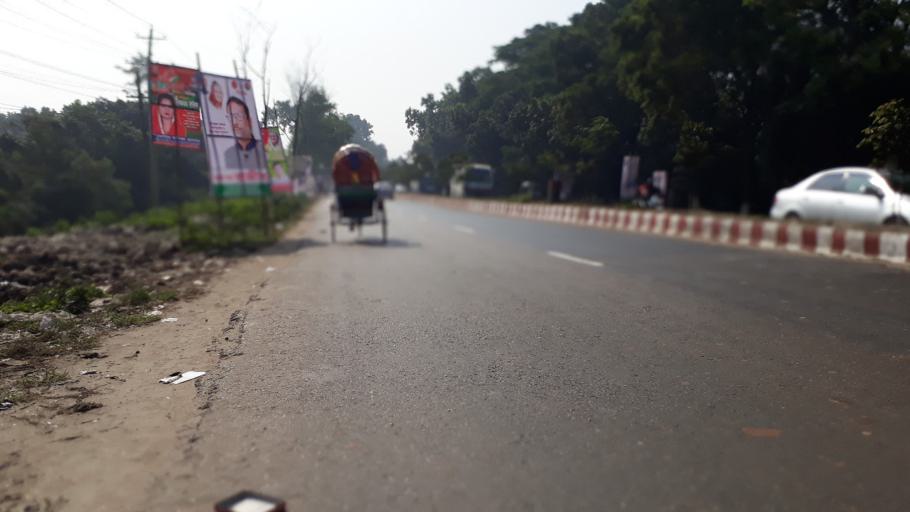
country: BD
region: Dhaka
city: Tungi
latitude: 23.8716
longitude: 90.2731
